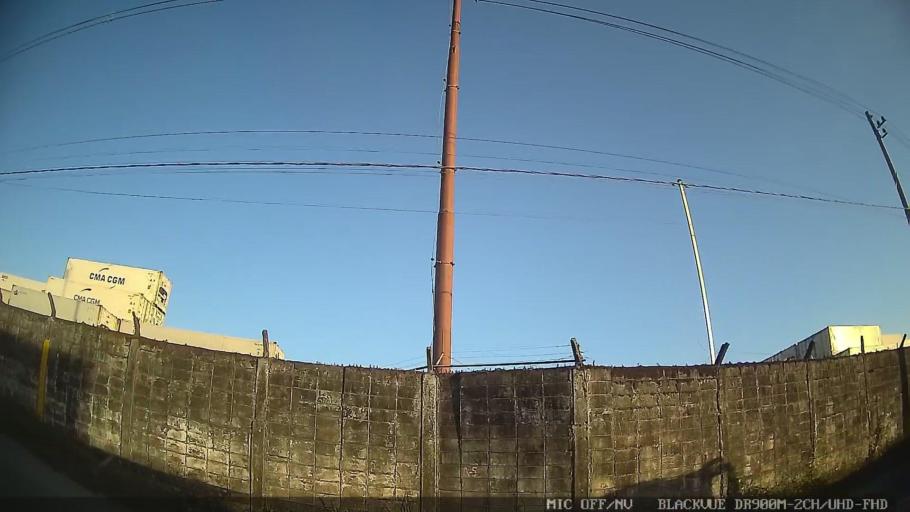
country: BR
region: Sao Paulo
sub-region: Guaruja
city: Guaruja
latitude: -23.9730
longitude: -46.2658
